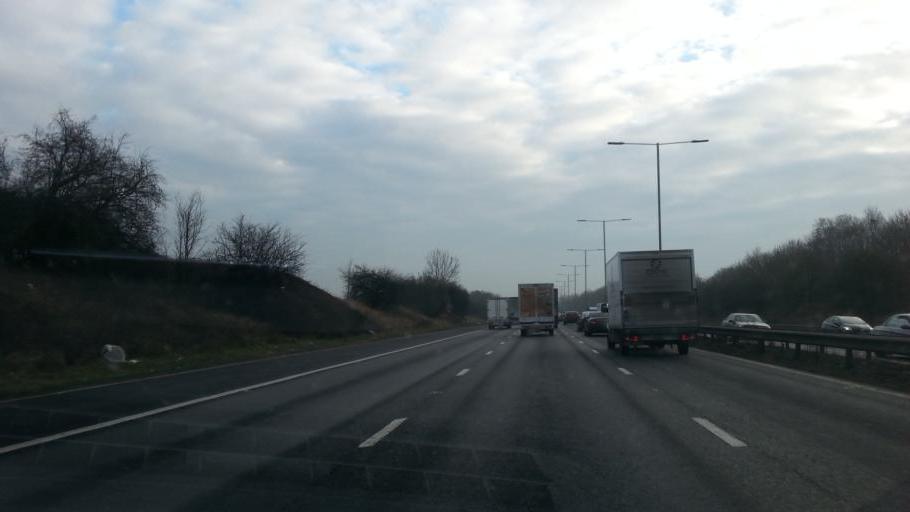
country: GB
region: England
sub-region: Warwickshire
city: Water Orton
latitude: 52.4971
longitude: -1.7367
